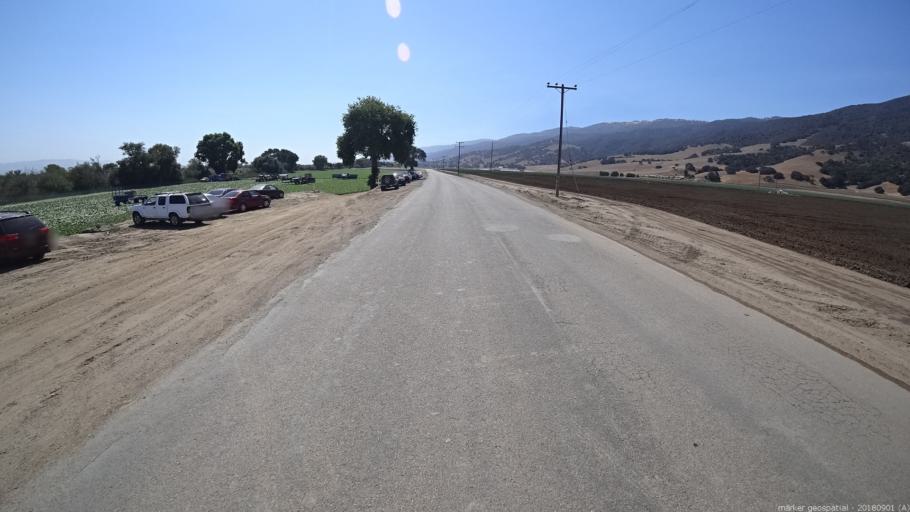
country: US
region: California
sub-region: Monterey County
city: Chualar
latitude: 36.5460
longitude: -121.5456
